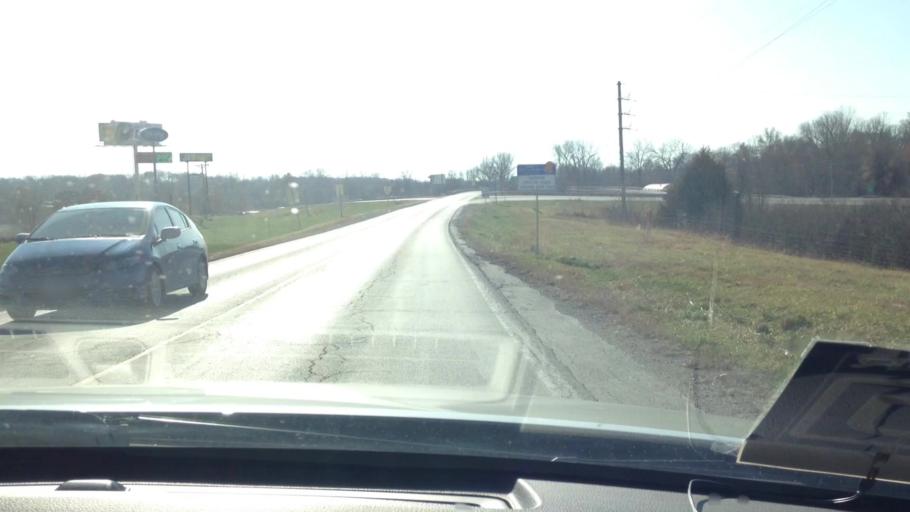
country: US
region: Missouri
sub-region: Platte County
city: Platte City
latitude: 39.5186
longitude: -94.7850
